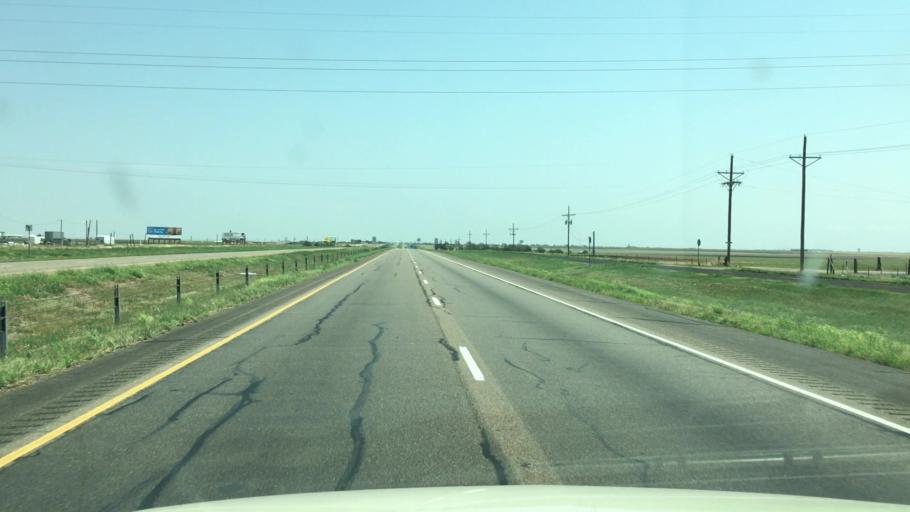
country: US
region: Texas
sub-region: Potter County
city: Bushland
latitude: 35.1908
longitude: -102.0472
